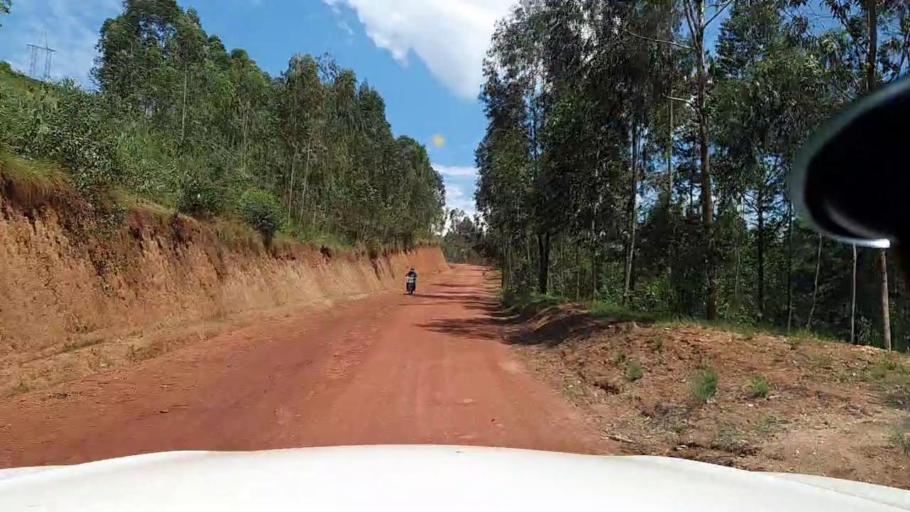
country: RW
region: Kigali
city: Kigali
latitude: -1.7679
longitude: 29.8738
